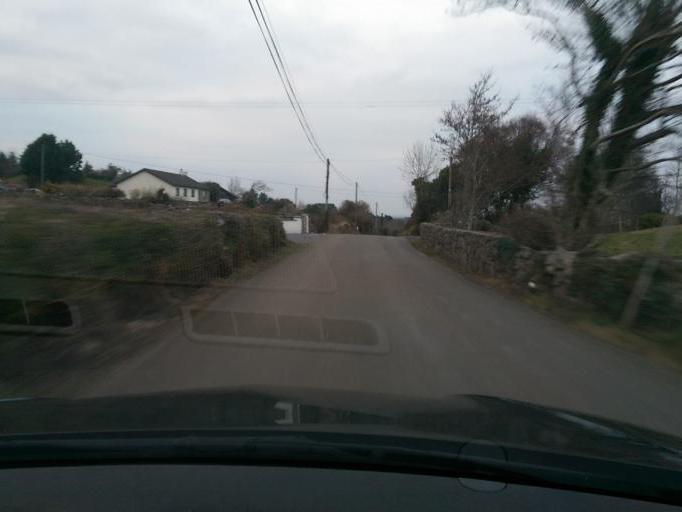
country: IE
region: Connaught
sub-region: County Galway
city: Bearna
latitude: 53.2943
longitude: -9.1632
